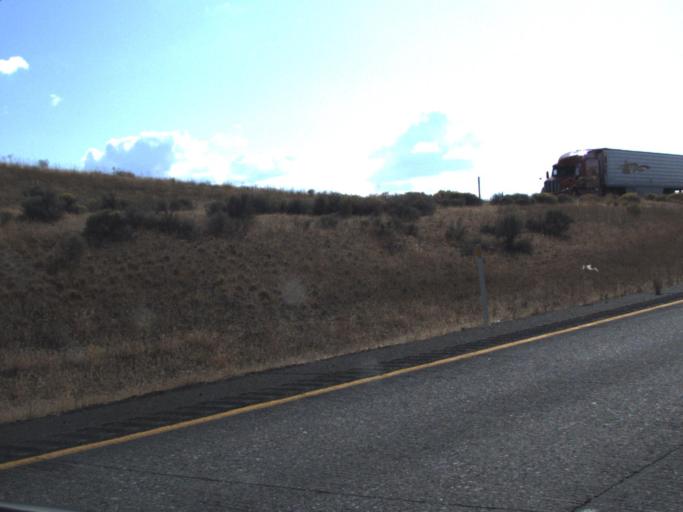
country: US
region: Oregon
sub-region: Umatilla County
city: Umatilla
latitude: 45.9848
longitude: -119.3103
